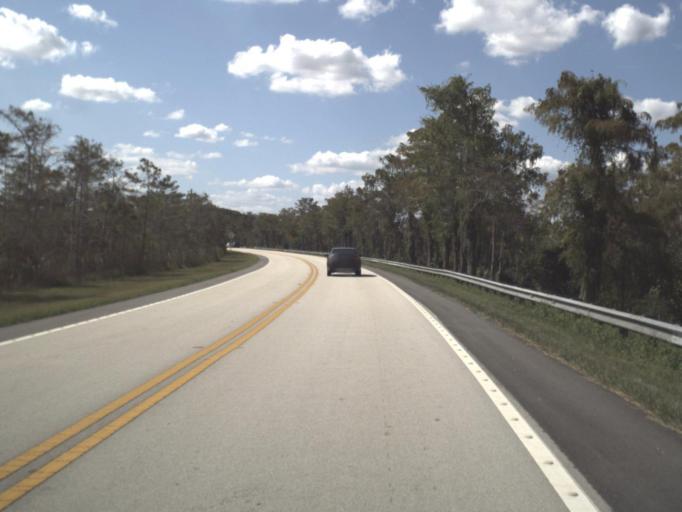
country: US
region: Florida
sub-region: Miami-Dade County
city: Kendall West
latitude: 25.8451
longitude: -80.9200
